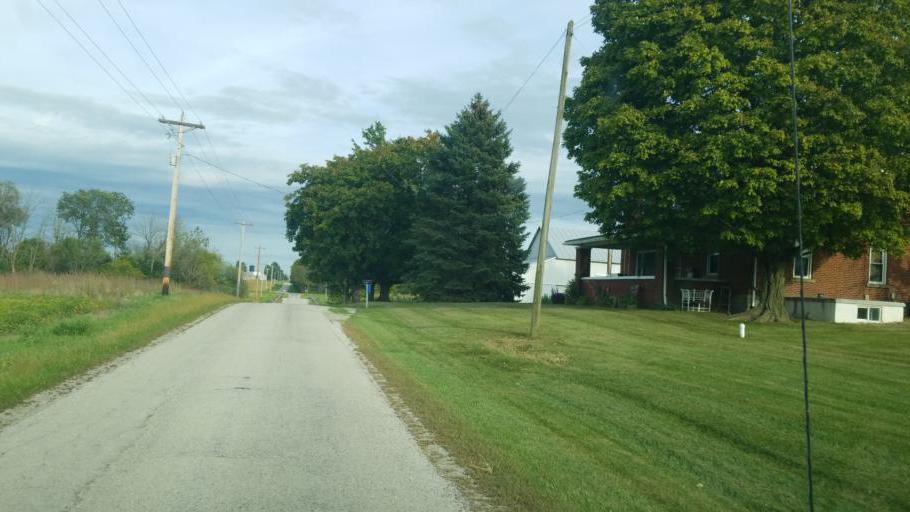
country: US
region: Ohio
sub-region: Crawford County
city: Bucyrus
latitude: 40.8776
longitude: -83.0591
